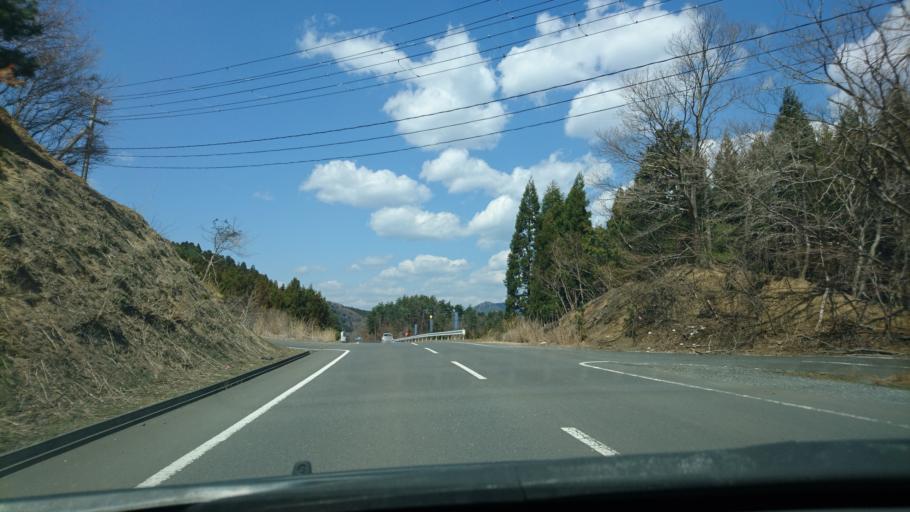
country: JP
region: Miyagi
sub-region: Oshika Gun
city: Onagawa Cho
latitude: 38.4783
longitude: 141.4936
